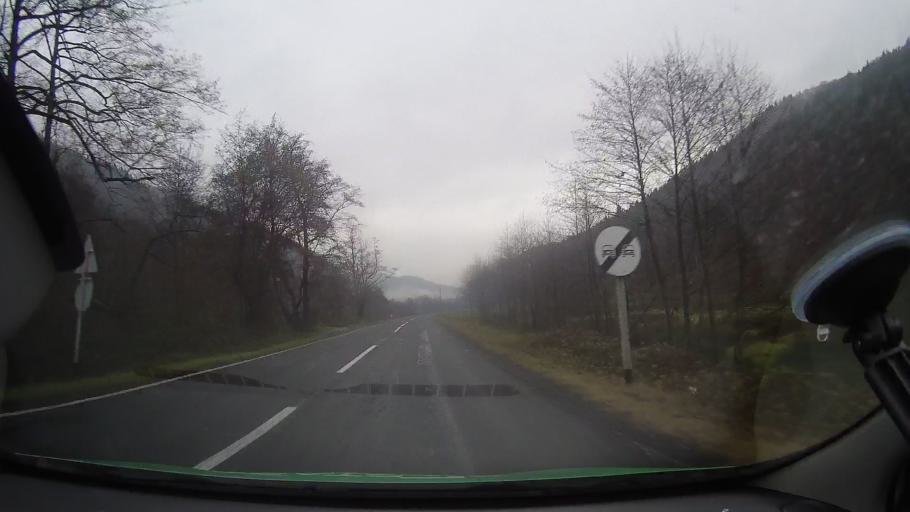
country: RO
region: Arad
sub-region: Comuna Plescuta
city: Plescuta
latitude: 46.3038
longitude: 22.4559
